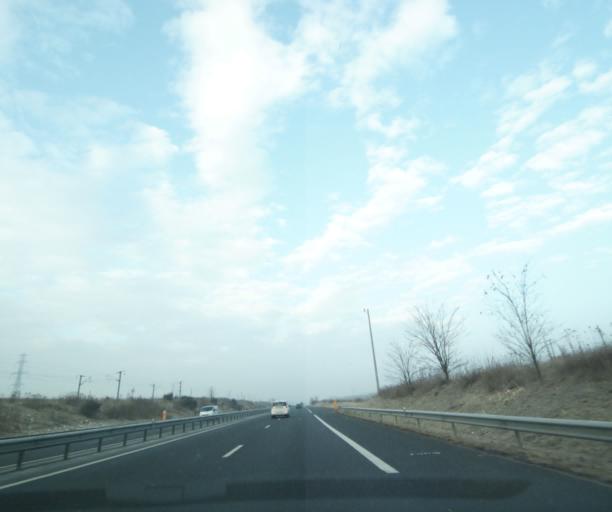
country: FR
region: Rhone-Alpes
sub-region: Departement de l'Ain
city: Beynost
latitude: 45.8569
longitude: 4.9926
